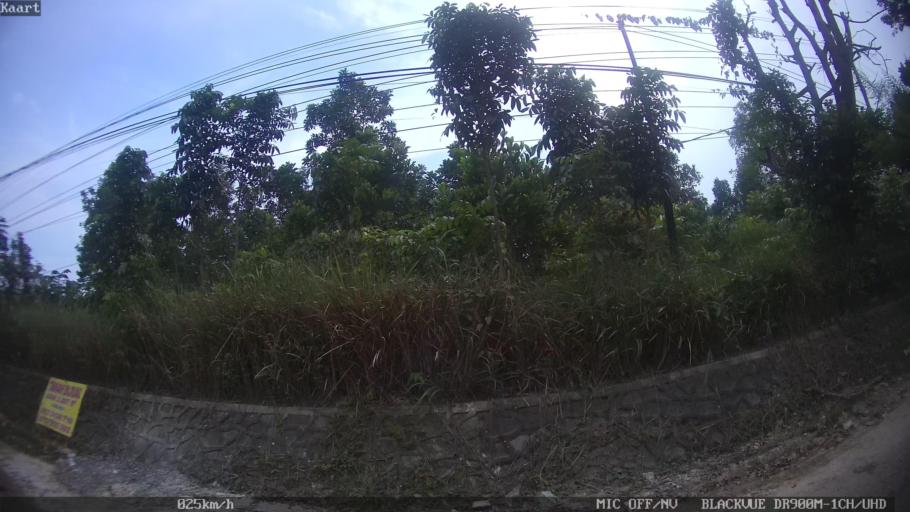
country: ID
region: Lampung
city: Panjang
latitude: -5.4130
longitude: 105.3214
